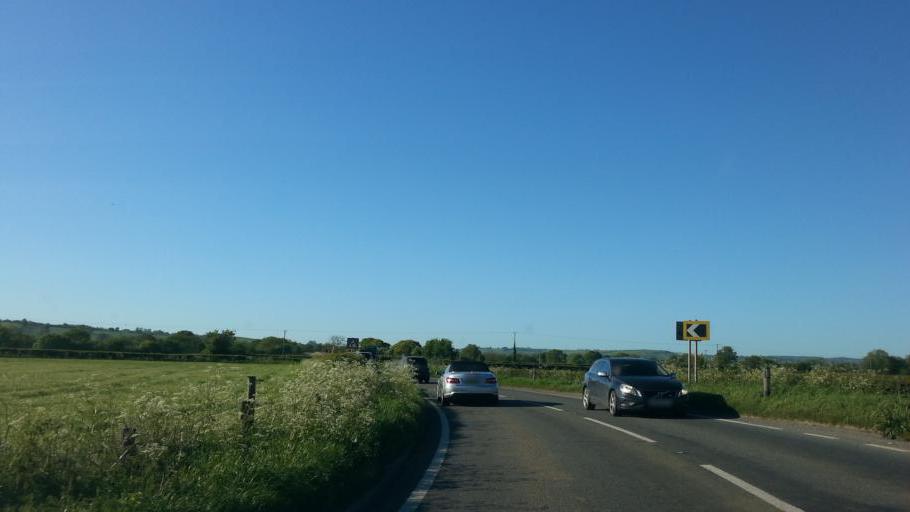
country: GB
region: England
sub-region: Somerset
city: Castle Cary
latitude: 51.1127
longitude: -2.5195
